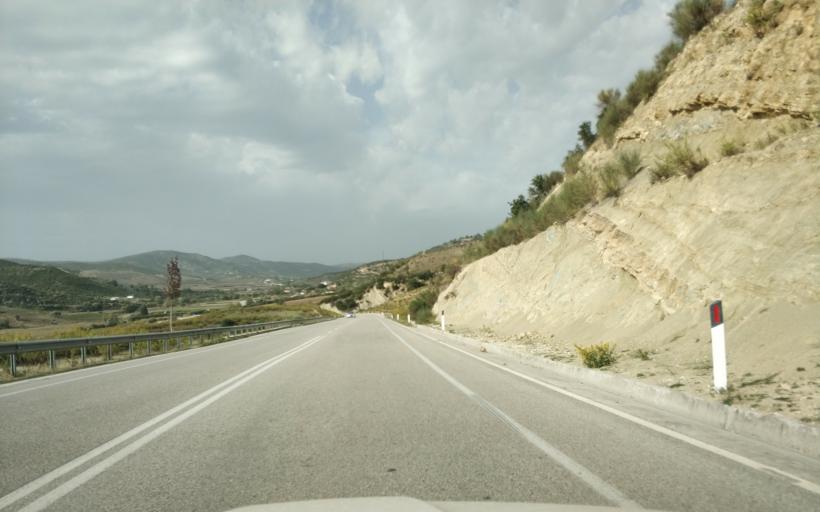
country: AL
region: Gjirokaster
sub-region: Rrethi i Tepelenes
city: Krahes
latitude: 40.4004
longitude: 19.8637
